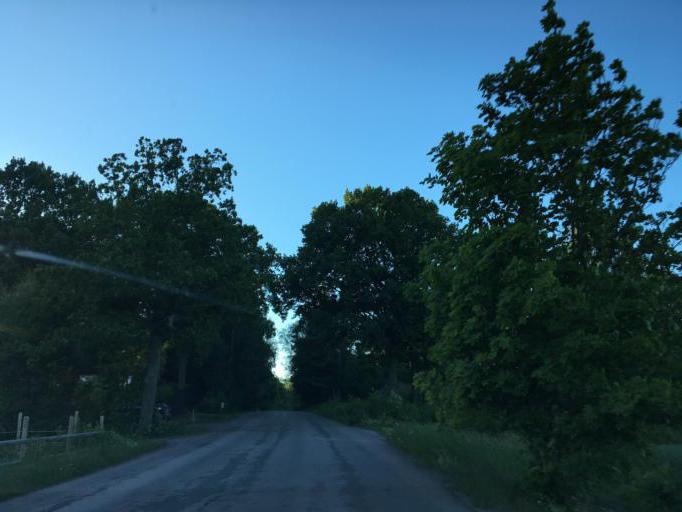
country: SE
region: Vaestmanland
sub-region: Vasteras
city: Vasteras
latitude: 59.5216
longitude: 16.5288
